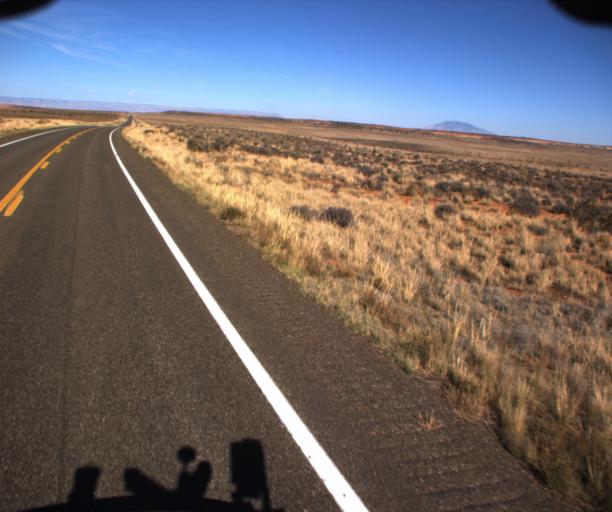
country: US
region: Arizona
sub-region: Coconino County
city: LeChee
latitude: 36.7536
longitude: -111.5730
